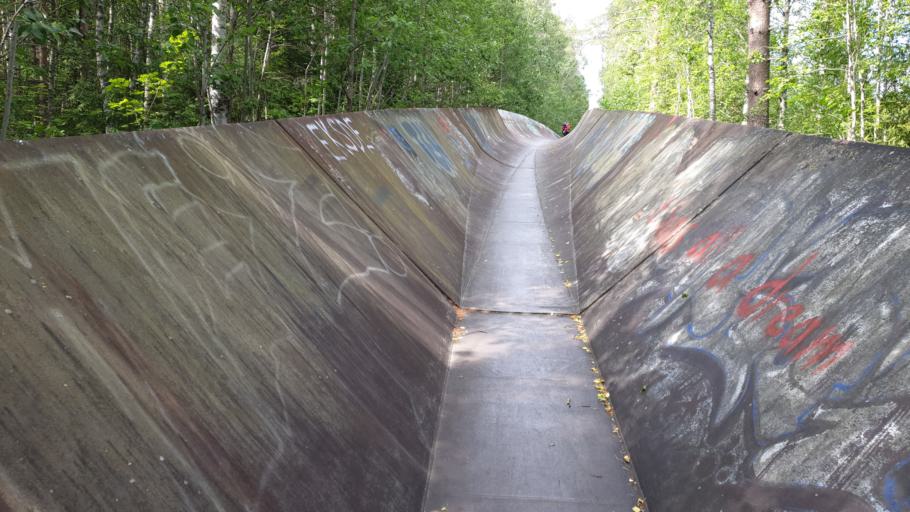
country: SE
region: Vaesterbotten
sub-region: Umea Kommun
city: Roback
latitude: 63.8330
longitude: 20.1259
